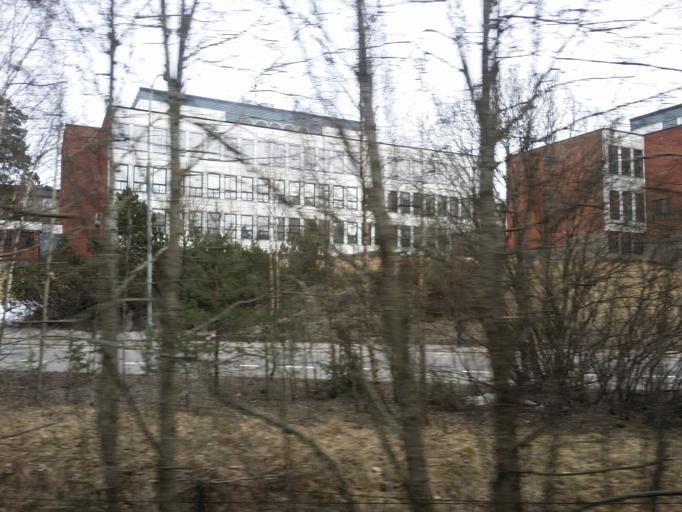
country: NO
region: Akershus
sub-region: Oppegard
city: Kolbotn
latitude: 59.8861
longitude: 10.8497
